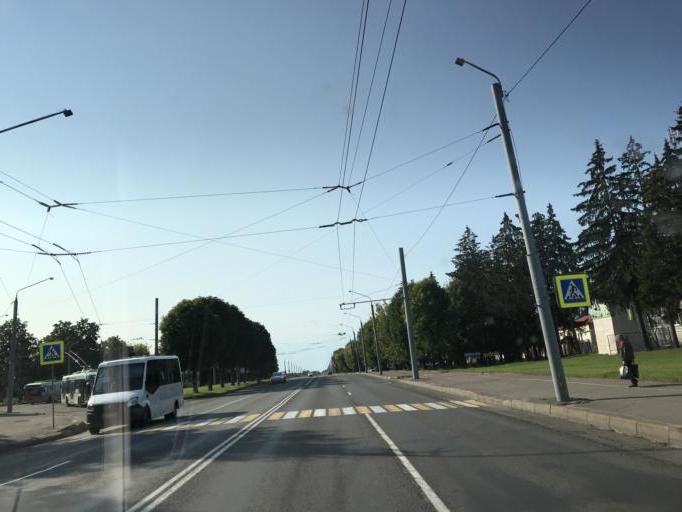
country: BY
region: Mogilev
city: Buynichy
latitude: 53.8786
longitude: 30.2660
